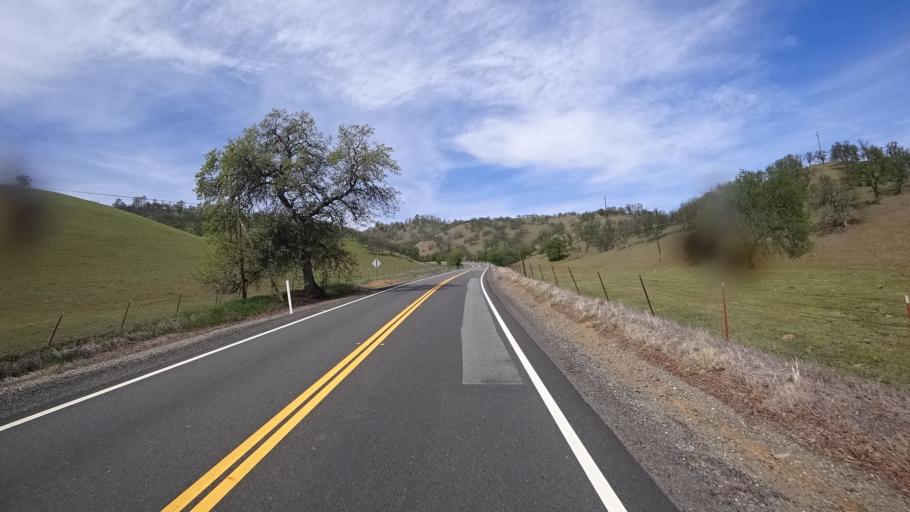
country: US
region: California
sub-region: Glenn County
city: Willows
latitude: 39.5969
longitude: -122.4925
